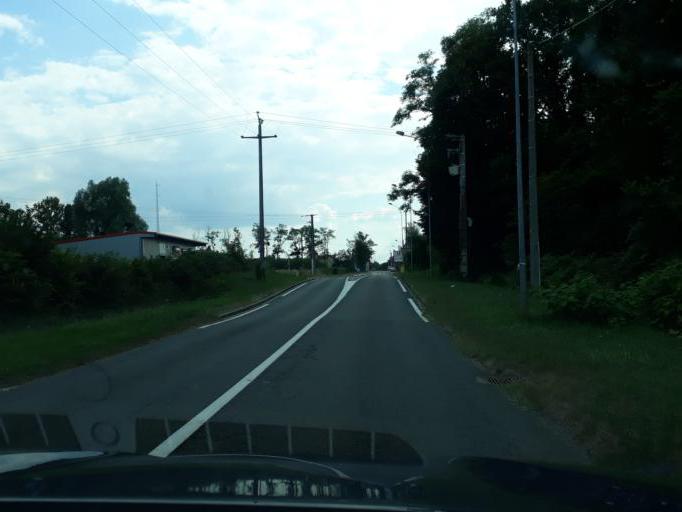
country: FR
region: Centre
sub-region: Departement du Cher
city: Jouet-sur-l'Aubois
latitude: 46.9599
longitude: 2.9584
